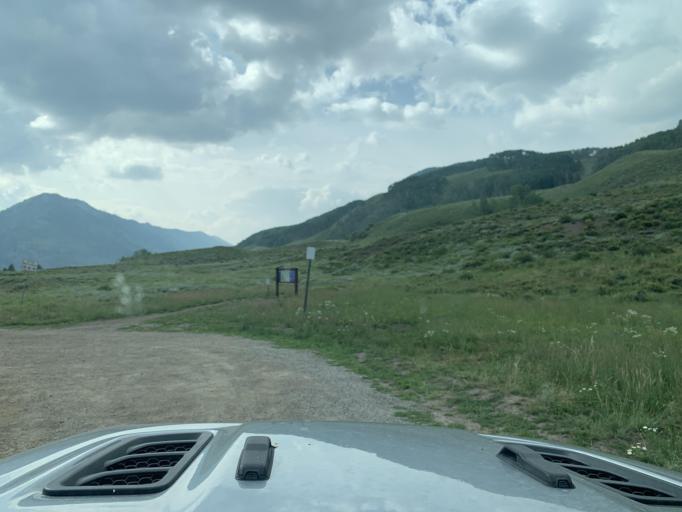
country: US
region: Colorado
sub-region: Gunnison County
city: Crested Butte
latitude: 38.9026
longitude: -107.0109
